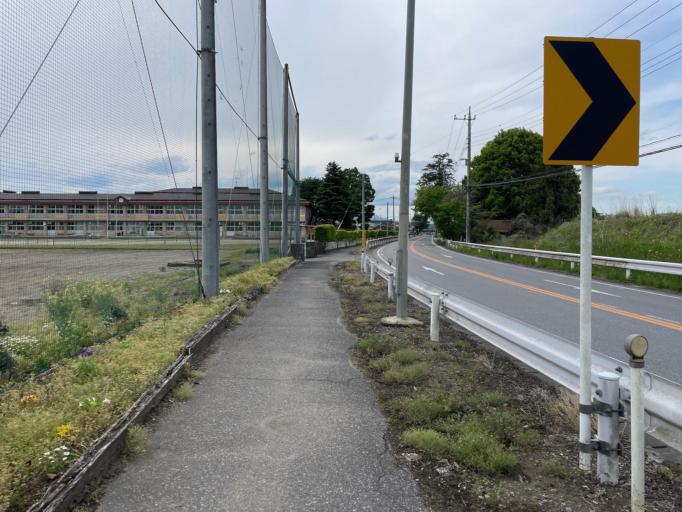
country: JP
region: Tochigi
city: Kanuma
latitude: 36.4929
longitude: 139.7554
